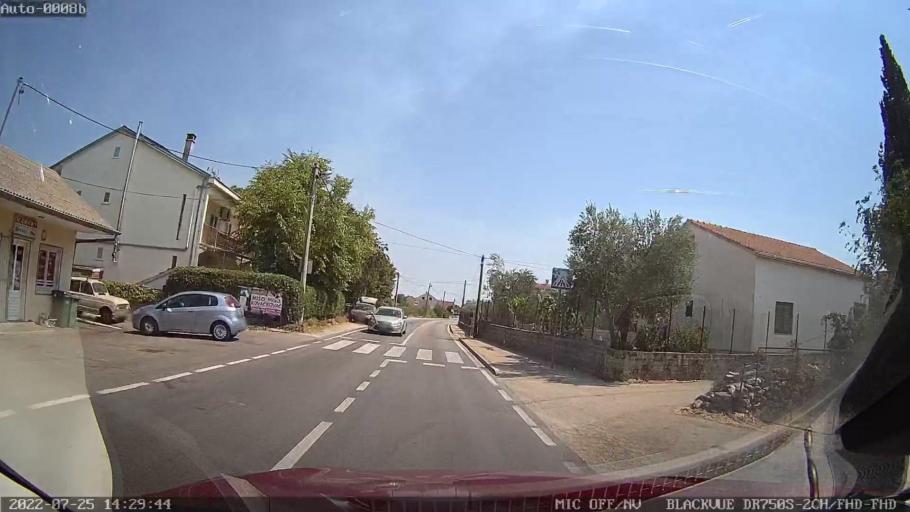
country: HR
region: Zadarska
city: Galovac
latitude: 44.1180
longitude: 15.3584
